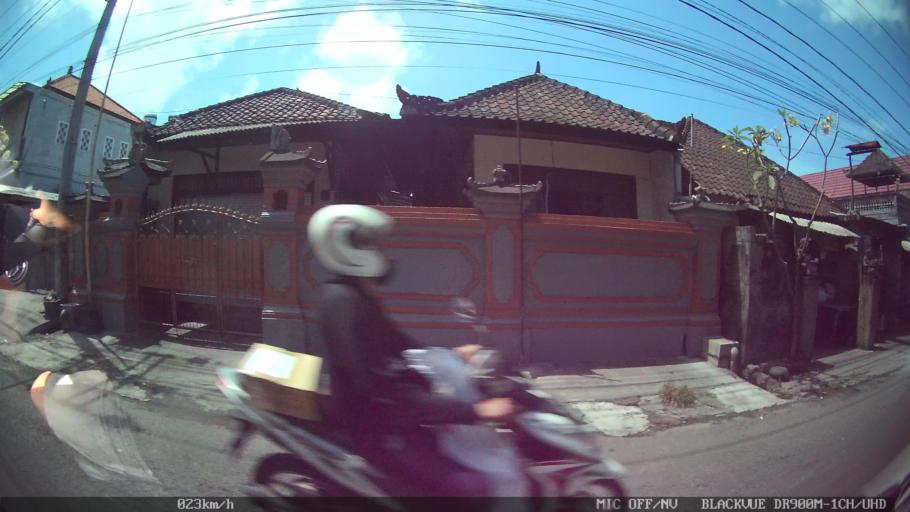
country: ID
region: Bali
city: Banjar Paangkelod
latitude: -8.6121
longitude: 115.2586
